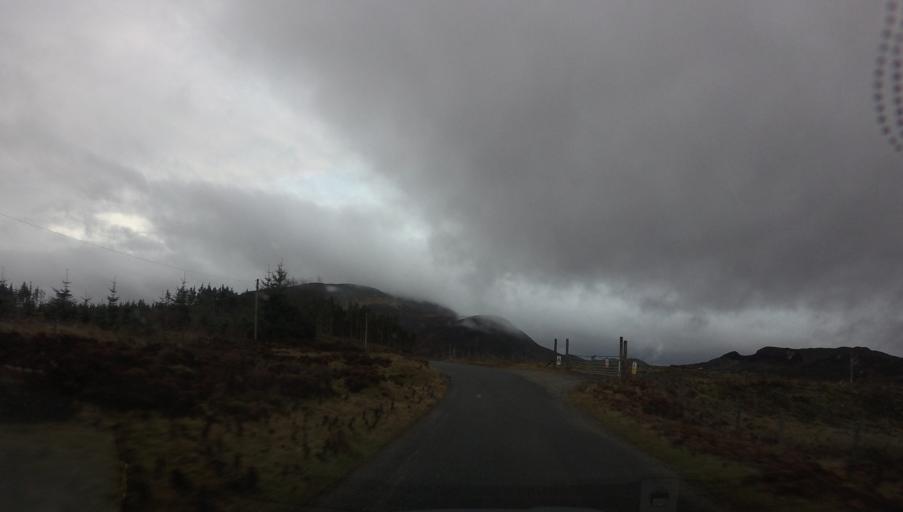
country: GB
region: Scotland
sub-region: Perth and Kinross
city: Aberfeldy
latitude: 56.6786
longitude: -4.0273
